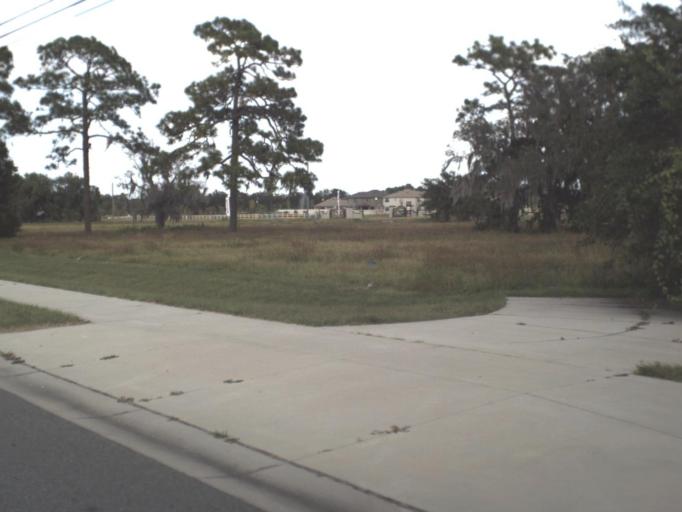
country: US
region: Florida
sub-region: Osceola County
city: Saint Cloud
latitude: 28.3010
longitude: -81.2390
